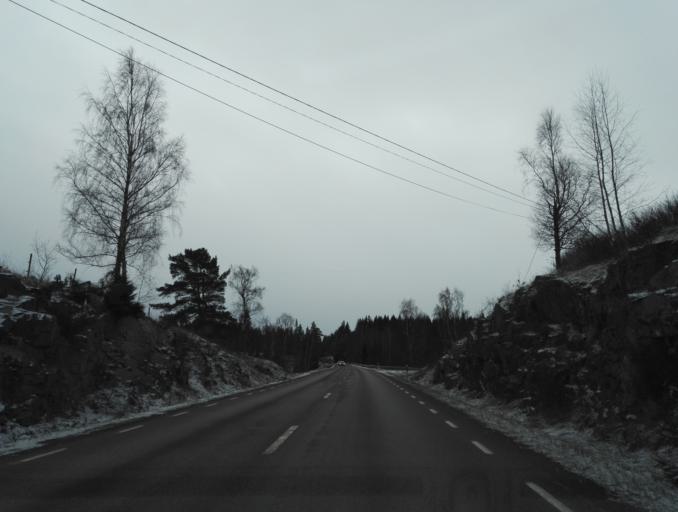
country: SE
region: Kalmar
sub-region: Hultsfreds Kommun
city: Virserum
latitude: 57.2853
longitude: 15.5660
